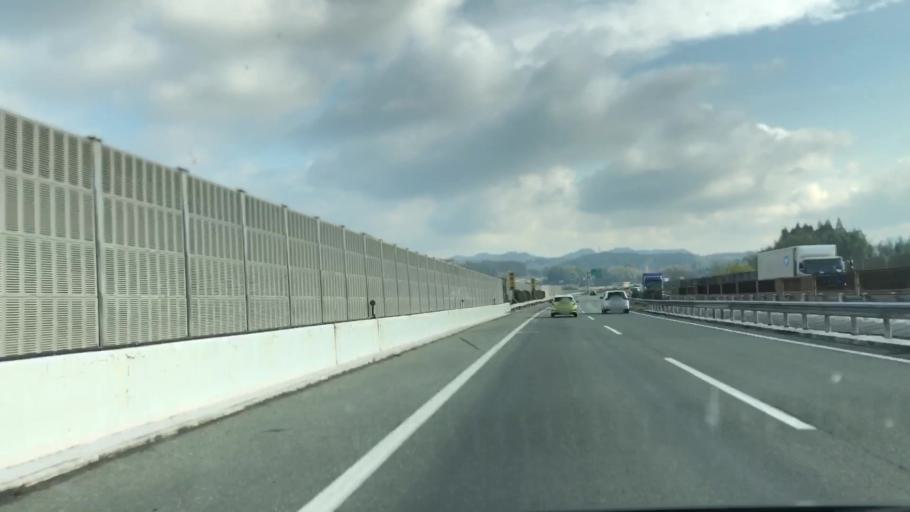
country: JP
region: Kumamoto
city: Tamana
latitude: 32.9967
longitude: 130.5959
